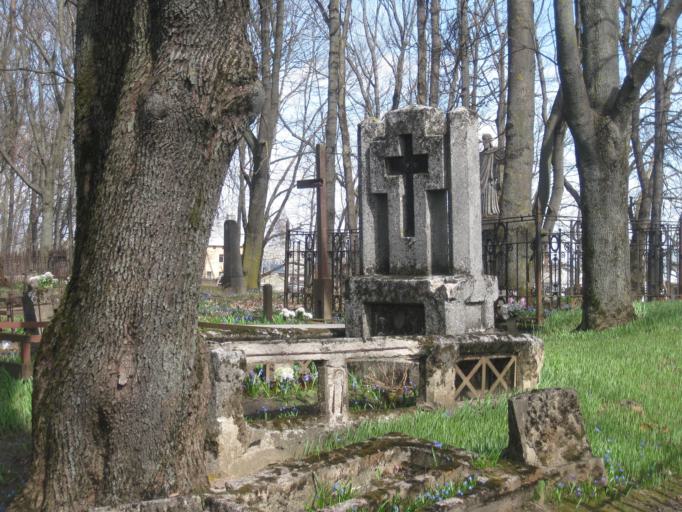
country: LT
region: Kauno apskritis
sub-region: Kaunas
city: Kaunas
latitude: 54.8984
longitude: 23.8855
